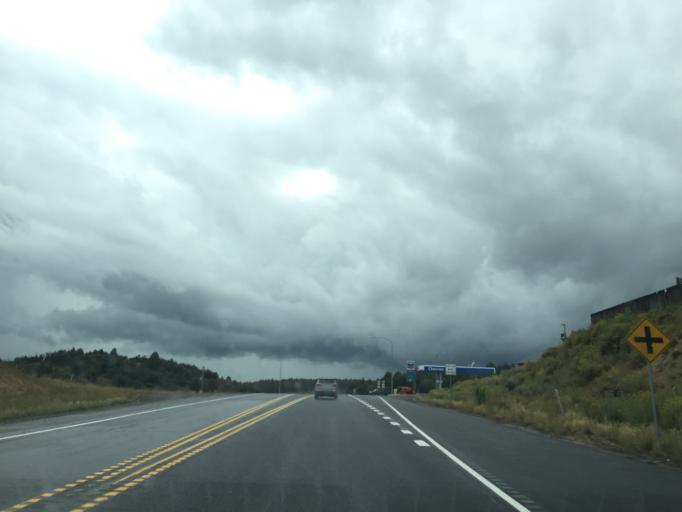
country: US
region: Utah
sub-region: Garfield County
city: Panguitch
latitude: 37.4901
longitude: -112.5117
